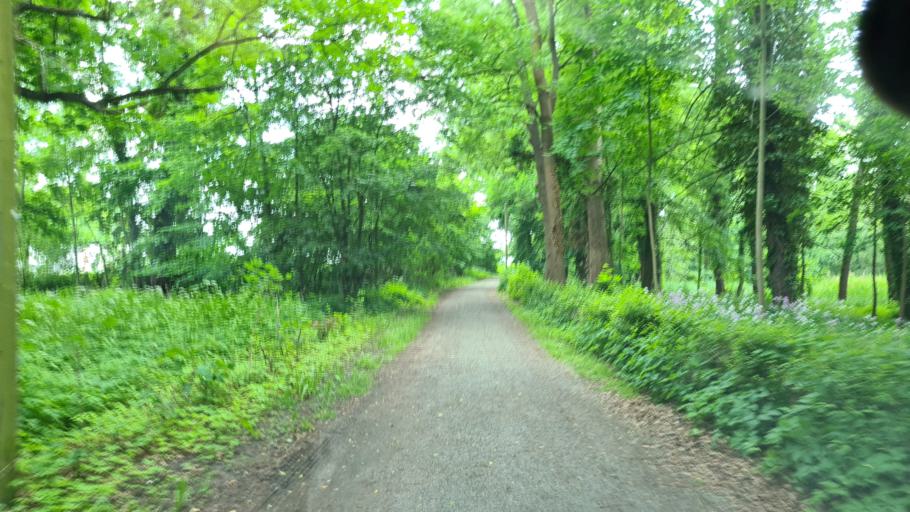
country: DE
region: Brandenburg
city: Sonnewalde
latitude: 51.6985
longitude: 13.6435
